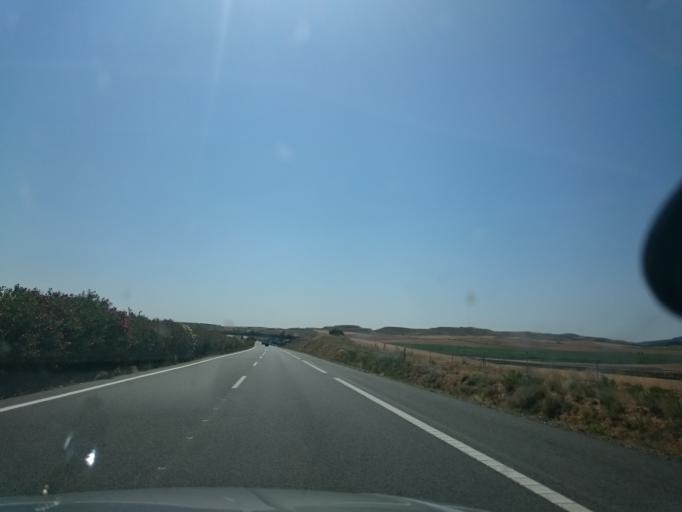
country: ES
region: Navarre
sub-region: Provincia de Navarra
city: Fontellas
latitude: 41.9854
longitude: -1.5679
